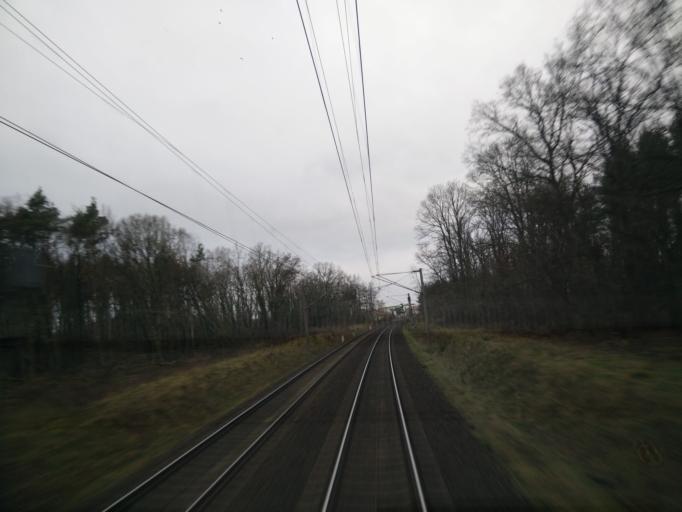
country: DE
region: Mecklenburg-Vorpommern
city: Ludwigslust
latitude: 53.3130
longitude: 11.5141
